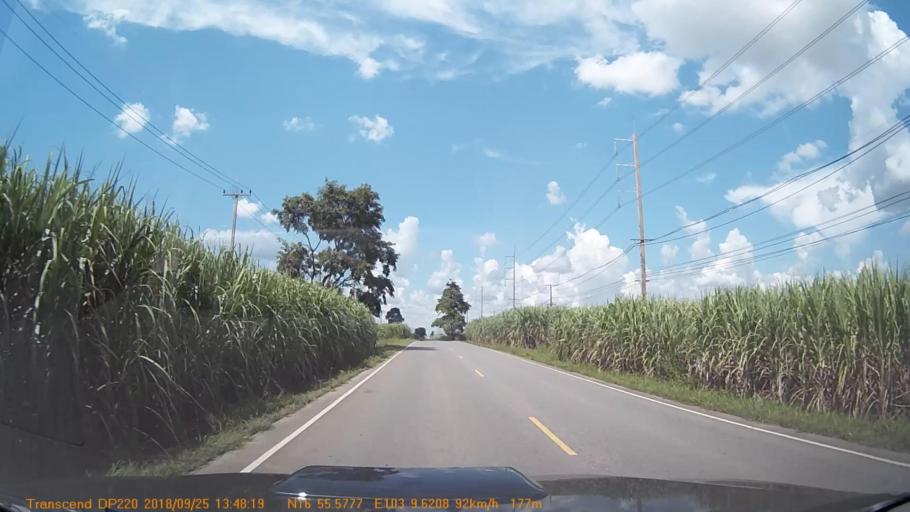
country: TH
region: Changwat Udon Thani
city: Si That
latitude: 16.9263
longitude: 103.1604
